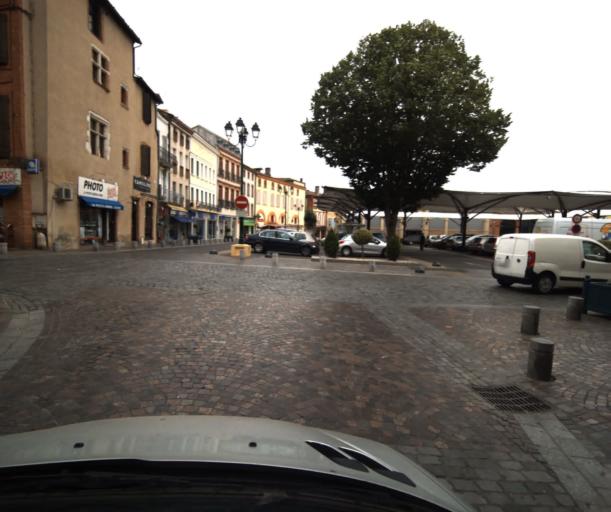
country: FR
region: Midi-Pyrenees
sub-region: Departement du Tarn-et-Garonne
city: Moissac
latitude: 44.1038
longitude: 1.0848
